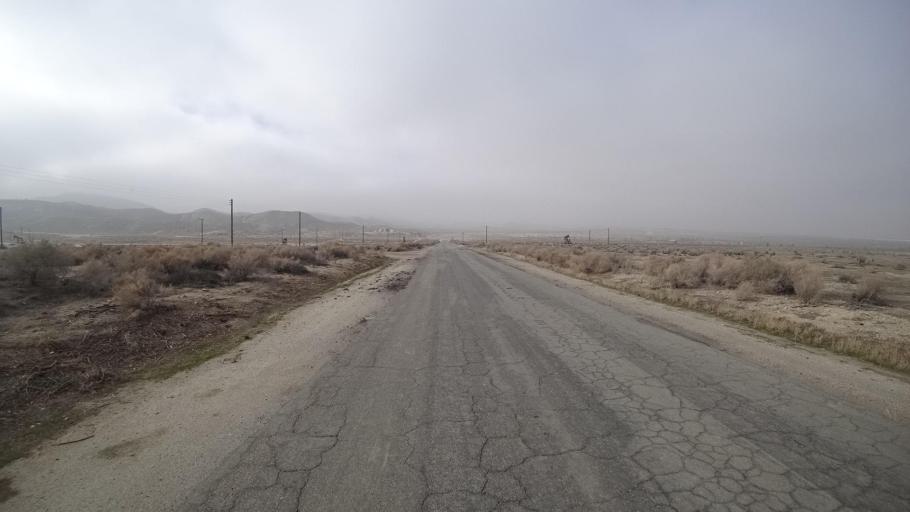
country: US
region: California
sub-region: Kern County
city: Maricopa
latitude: 35.0379
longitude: -119.3689
